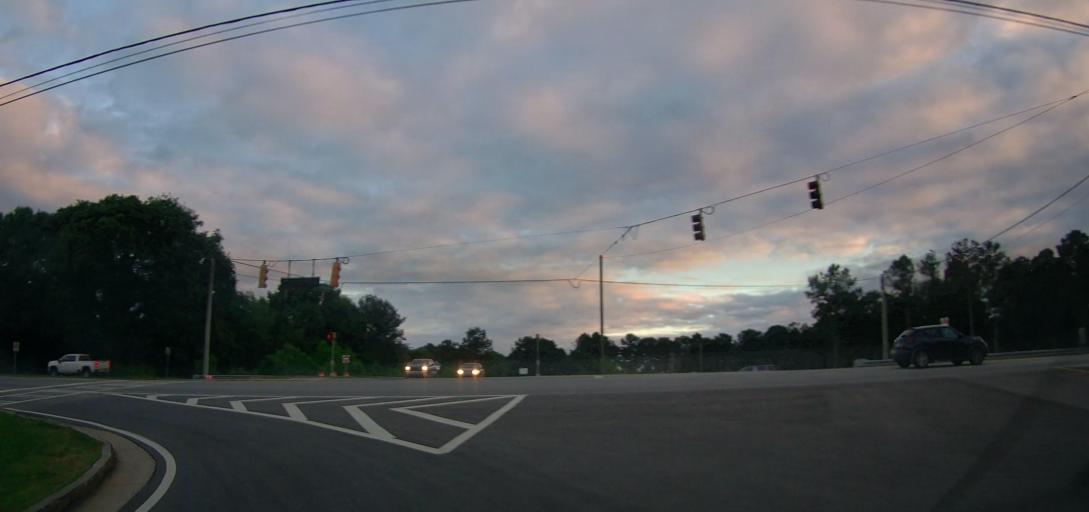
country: US
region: Georgia
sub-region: Clarke County
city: Country Club Estates
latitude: 33.9397
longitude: -83.4606
